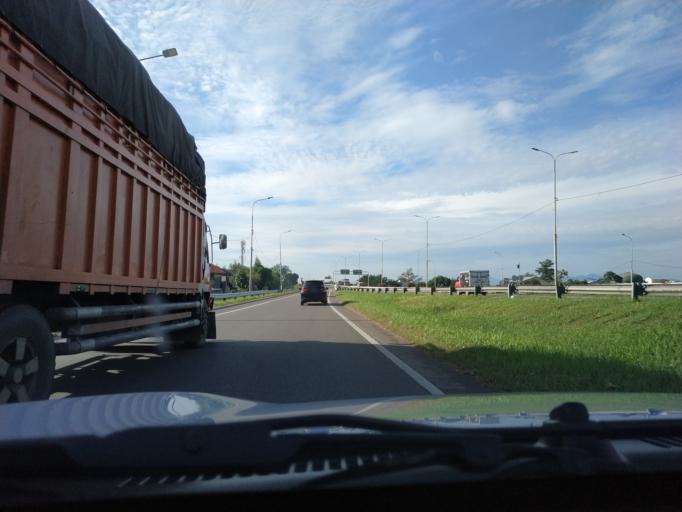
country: ID
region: North Sumatra
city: Medan
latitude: 3.5948
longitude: 98.7242
